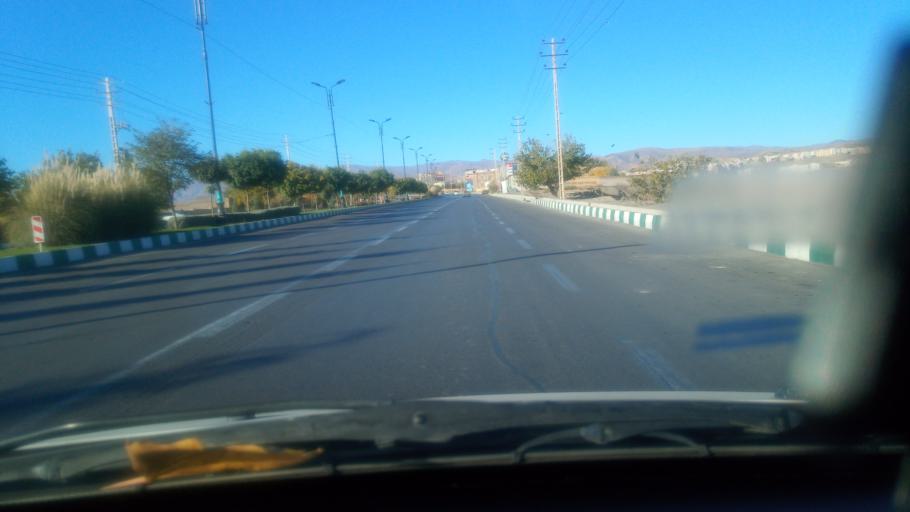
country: IR
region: Razavi Khorasan
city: Torqabeh
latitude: 36.3176
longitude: 59.3862
